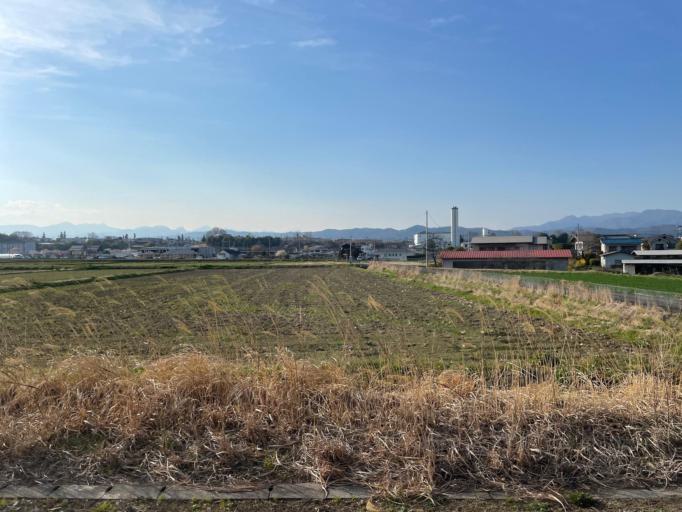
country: JP
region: Gunma
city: Annaka
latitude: 36.3137
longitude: 138.8845
